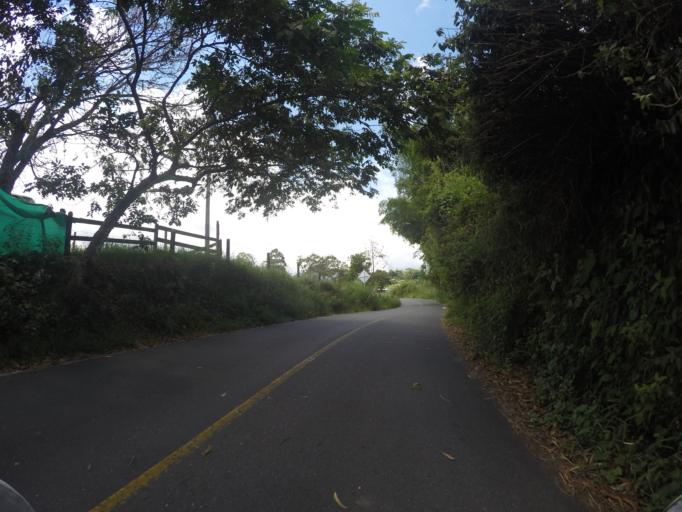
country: CO
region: Quindio
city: Filandia
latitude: 4.6328
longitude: -75.6948
